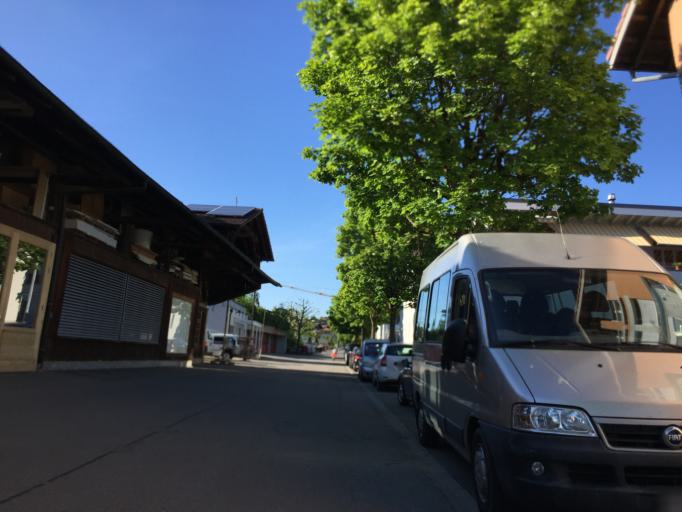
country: CH
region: Bern
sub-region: Bern-Mittelland District
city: Zaziwil
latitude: 46.9003
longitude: 7.6360
